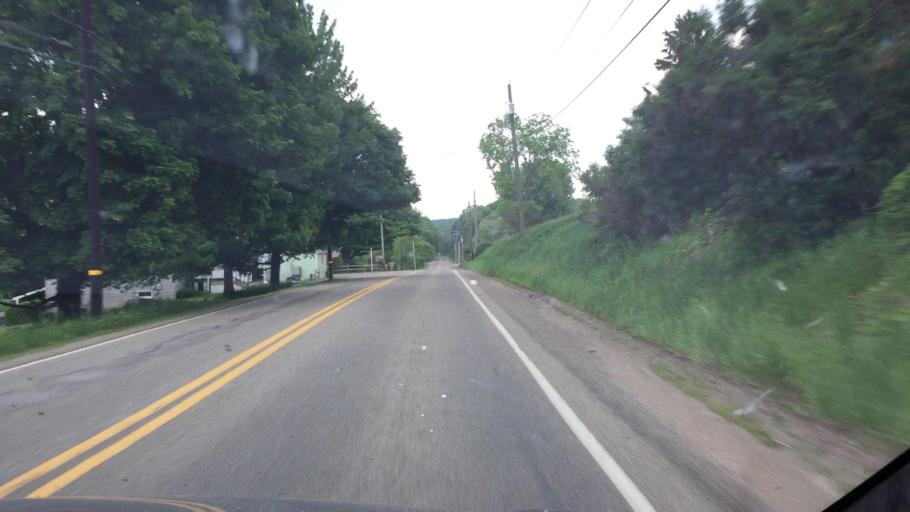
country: US
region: Pennsylvania
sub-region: Butler County
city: Slippery Rock
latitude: 41.0195
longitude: -80.0129
